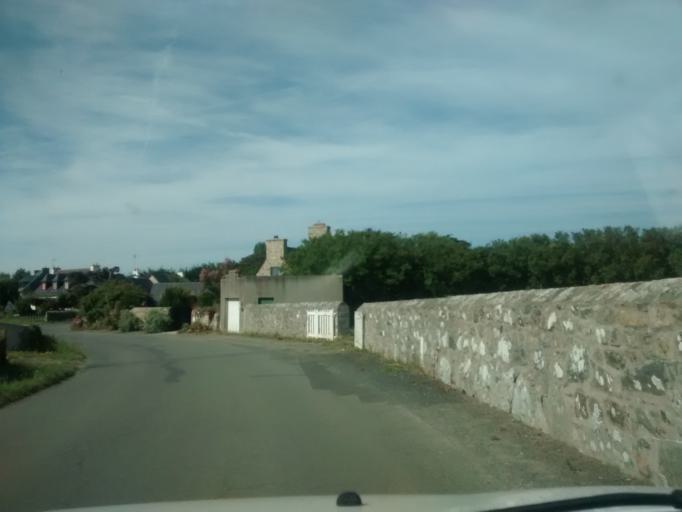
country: FR
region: Brittany
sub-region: Departement des Cotes-d'Armor
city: Plougrescant
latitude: 48.8605
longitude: -3.2303
